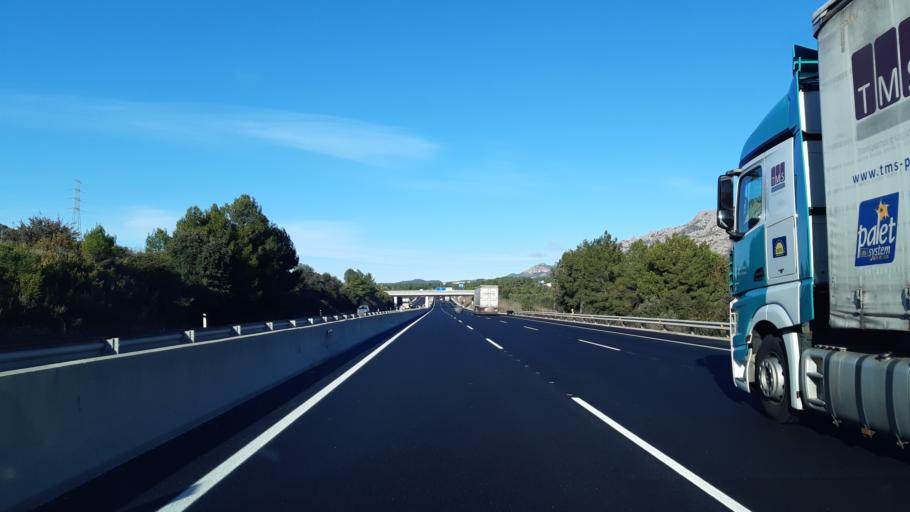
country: ES
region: Catalonia
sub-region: Provincia de Barcelona
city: Collbato
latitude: 41.5508
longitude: 1.8454
